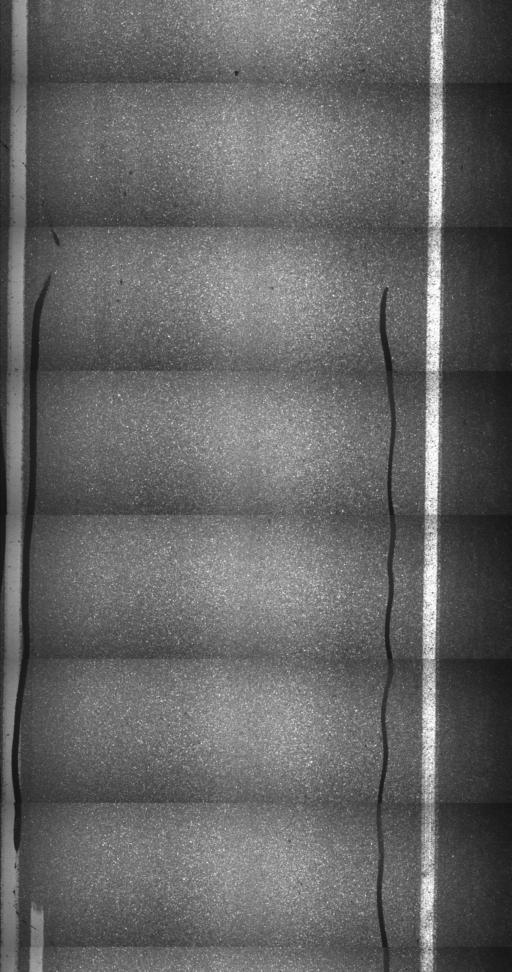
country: US
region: Vermont
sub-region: Windham County
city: Newfane
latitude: 43.0513
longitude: -72.6975
